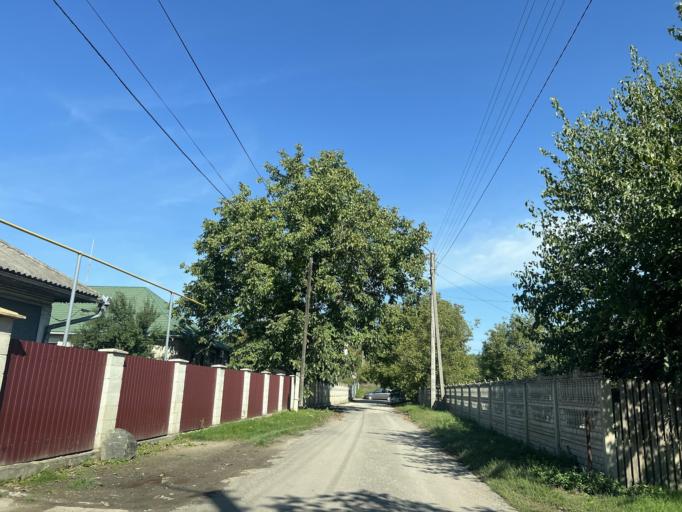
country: RO
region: Iasi
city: Ungheni-Prut
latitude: 47.1986
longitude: 27.7891
